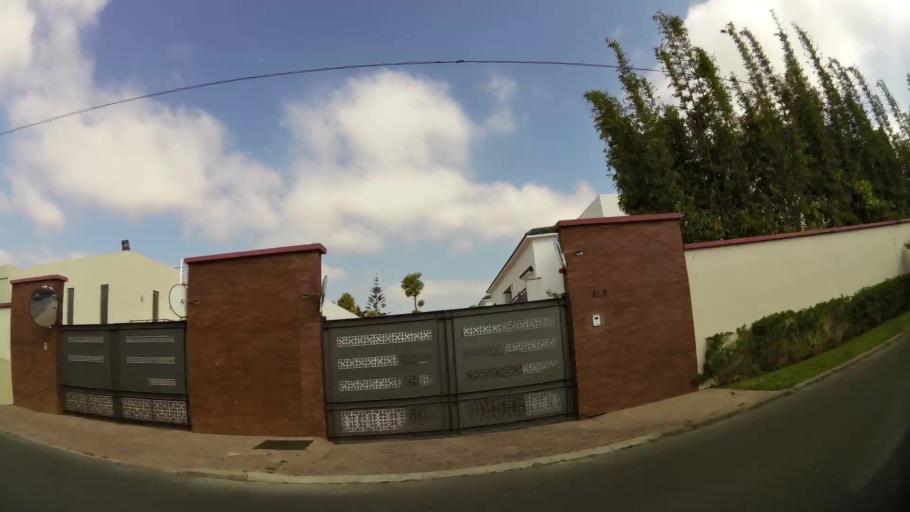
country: MA
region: Rabat-Sale-Zemmour-Zaer
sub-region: Rabat
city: Rabat
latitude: 33.9724
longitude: -6.8558
